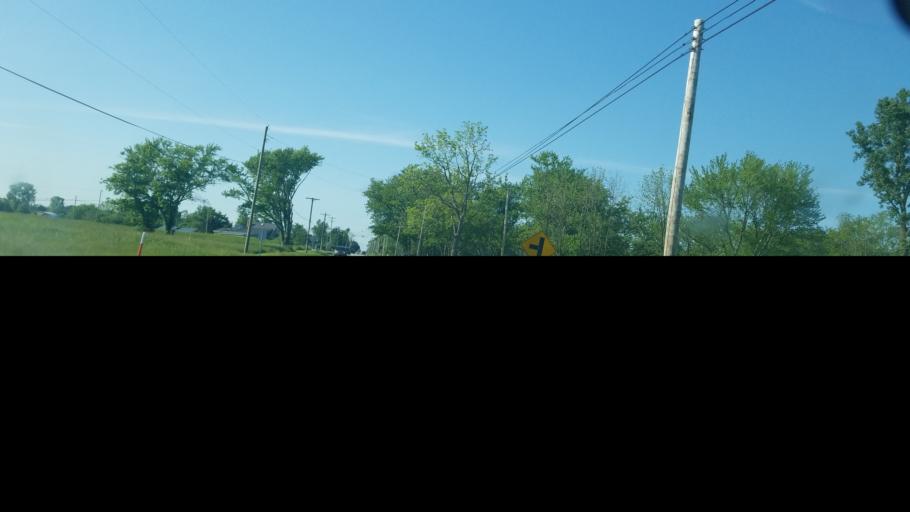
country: US
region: Ohio
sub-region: Medina County
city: Medina
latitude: 41.0746
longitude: -81.8643
